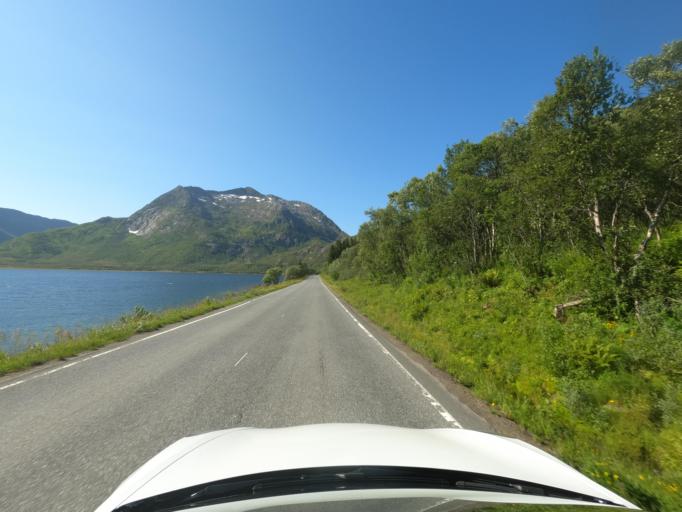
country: NO
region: Nordland
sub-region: Lodingen
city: Lodingen
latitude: 68.5460
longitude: 15.7414
